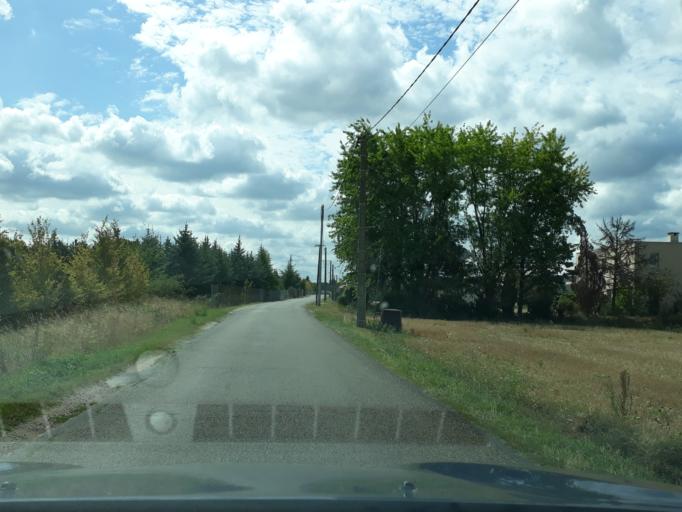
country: FR
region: Centre
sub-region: Departement du Loiret
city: Saint-Cyr-en-Val
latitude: 47.8462
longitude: 1.9738
